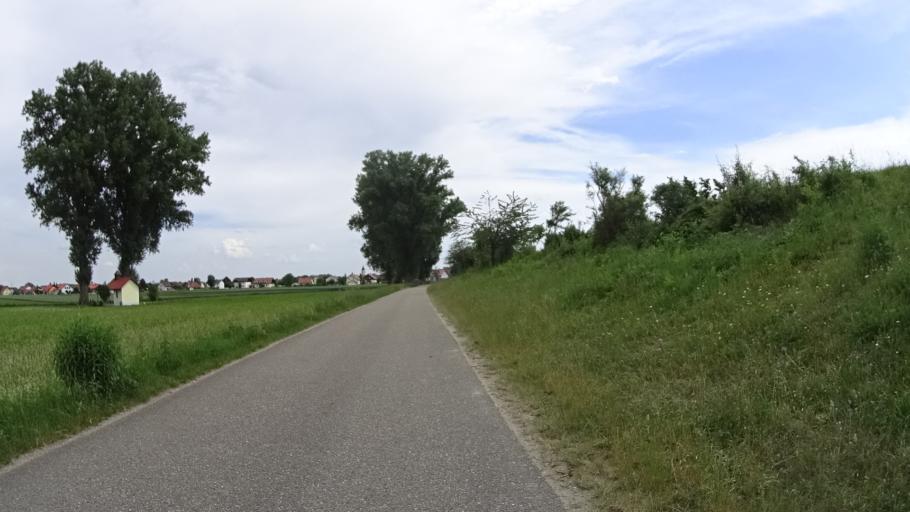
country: DE
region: Bavaria
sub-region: Upper Palatinate
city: Donaustauf
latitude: 49.0179
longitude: 12.2622
